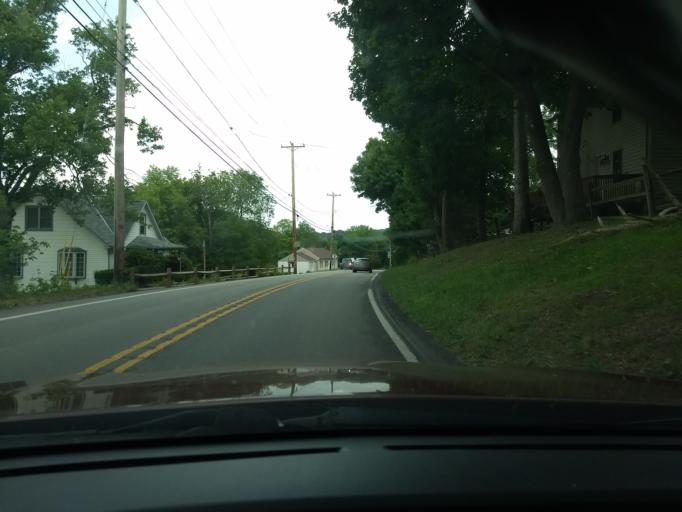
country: US
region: Pennsylvania
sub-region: Allegheny County
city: Bakerstown
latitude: 40.6516
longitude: -79.9410
